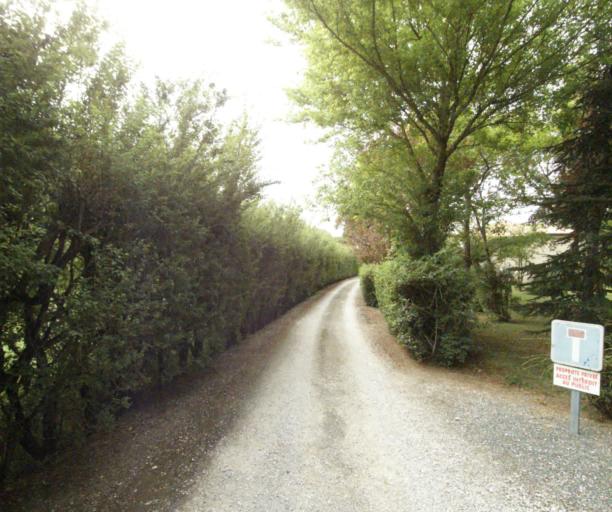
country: FR
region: Midi-Pyrenees
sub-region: Departement du Tarn
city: Soreze
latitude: 43.4562
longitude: 2.0688
